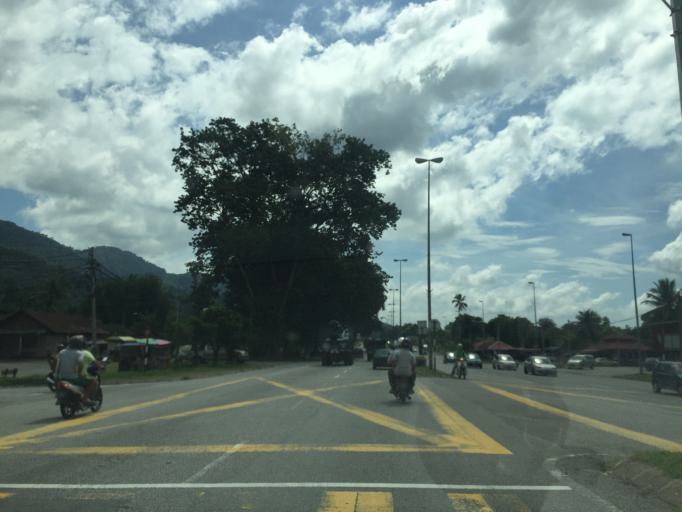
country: MY
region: Perak
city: Kampar
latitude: 4.3045
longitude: 101.1566
